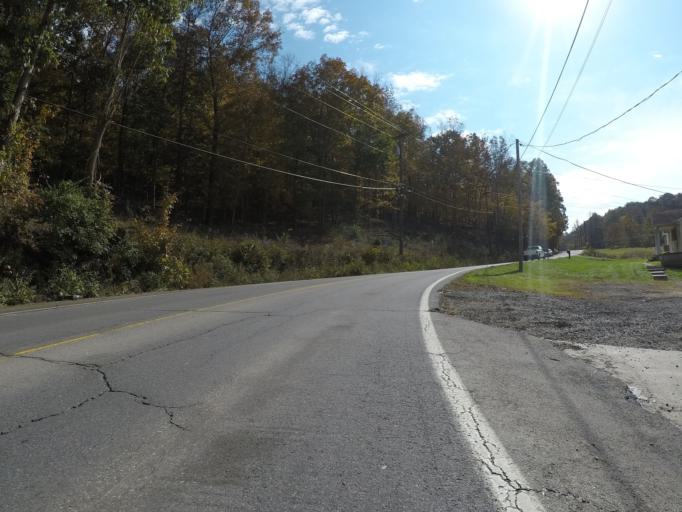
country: US
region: West Virginia
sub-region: Cabell County
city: Pea Ridge
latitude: 38.3862
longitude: -82.3794
